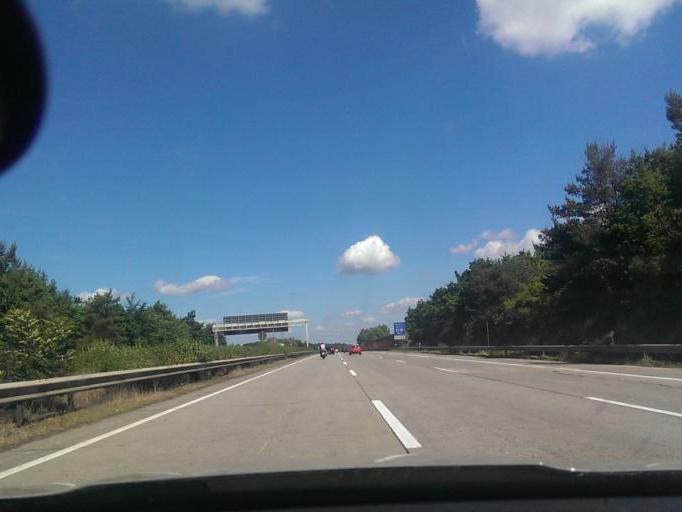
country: DE
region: Lower Saxony
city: Essel
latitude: 52.6839
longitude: 9.6899
